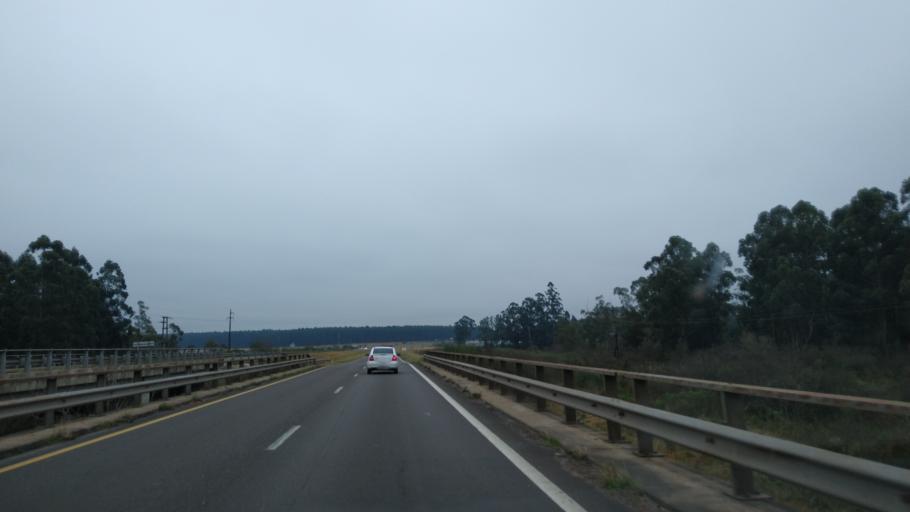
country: AR
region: Entre Rios
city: Chajari
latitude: -30.8397
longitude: -58.0488
